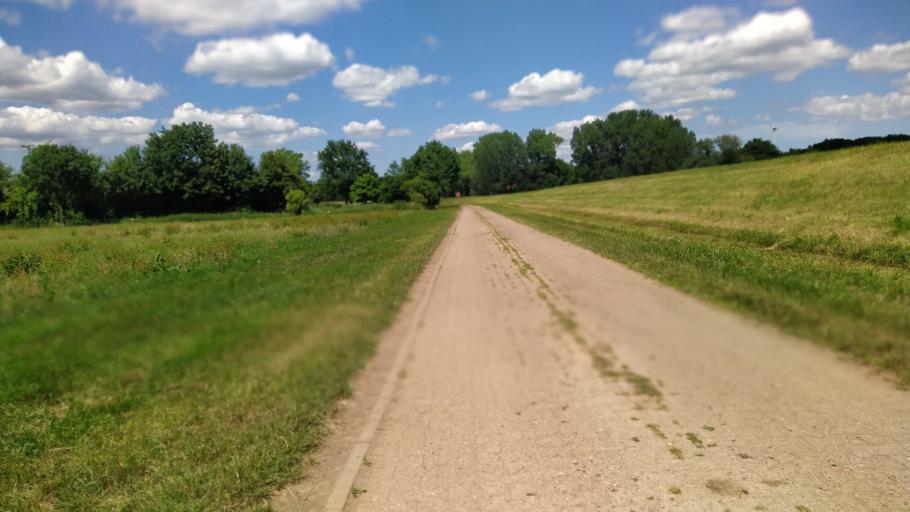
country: DE
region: Lower Saxony
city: Estorf
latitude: 53.5705
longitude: 9.1681
